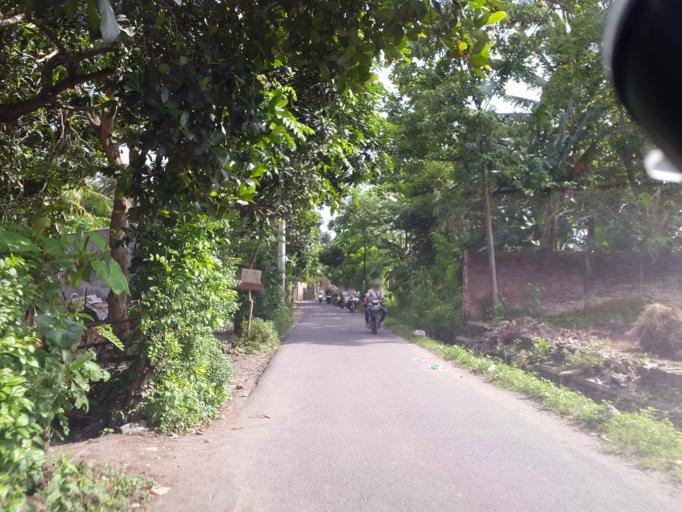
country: ID
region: West Nusa Tenggara
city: Mambalan
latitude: -8.5399
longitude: 116.0907
